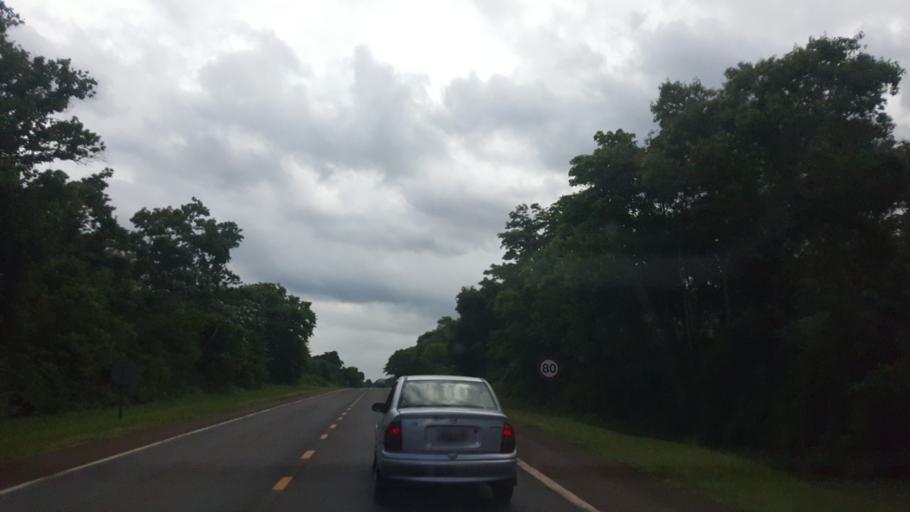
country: AR
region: Misiones
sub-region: Departamento de Iguazu
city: Puerto Iguazu
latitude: -25.7267
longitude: -54.5287
